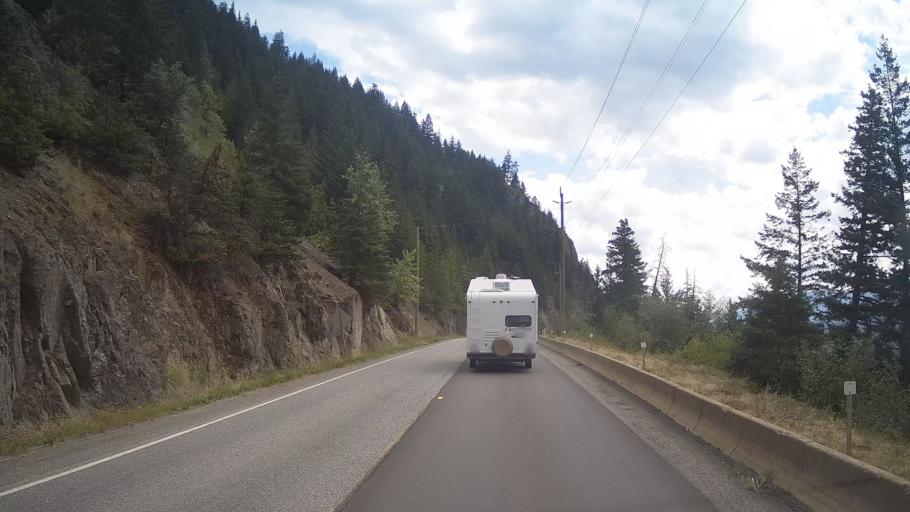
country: CA
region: British Columbia
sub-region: Thompson-Nicola Regional District
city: Ashcroft
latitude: 50.0843
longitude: -121.5531
